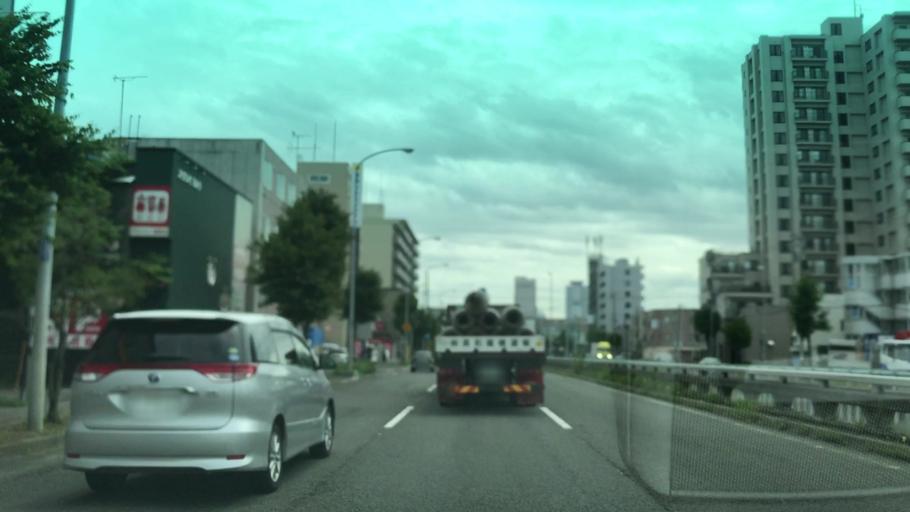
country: JP
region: Hokkaido
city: Sapporo
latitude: 43.0869
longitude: 141.3488
